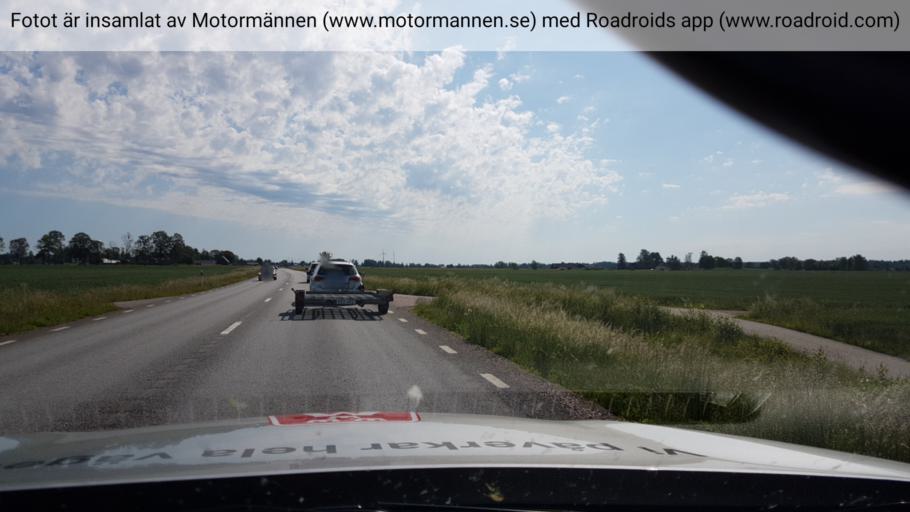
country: SE
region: OErebro
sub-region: Orebro Kommun
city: Odensbacken
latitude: 59.1532
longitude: 15.4997
